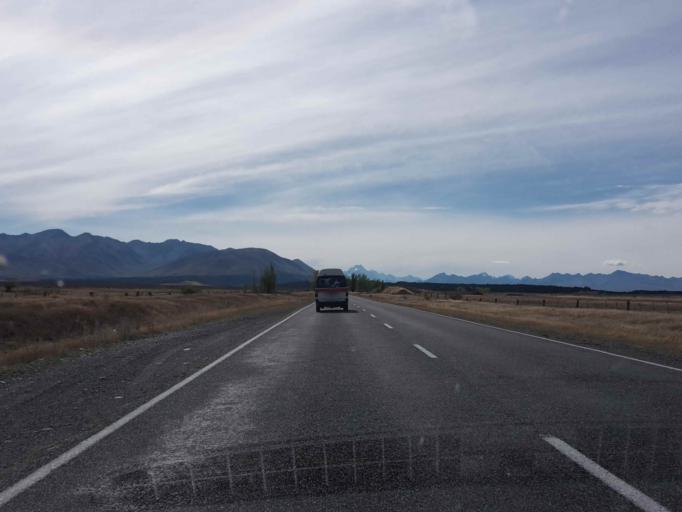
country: NZ
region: Canterbury
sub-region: Timaru District
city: Pleasant Point
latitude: -44.2255
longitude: 170.1164
